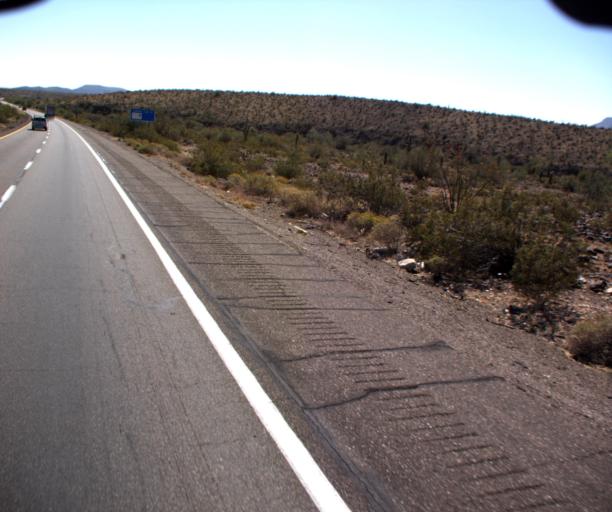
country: US
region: Arizona
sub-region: La Paz County
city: Quartzsite
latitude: 33.6641
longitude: -114.0301
